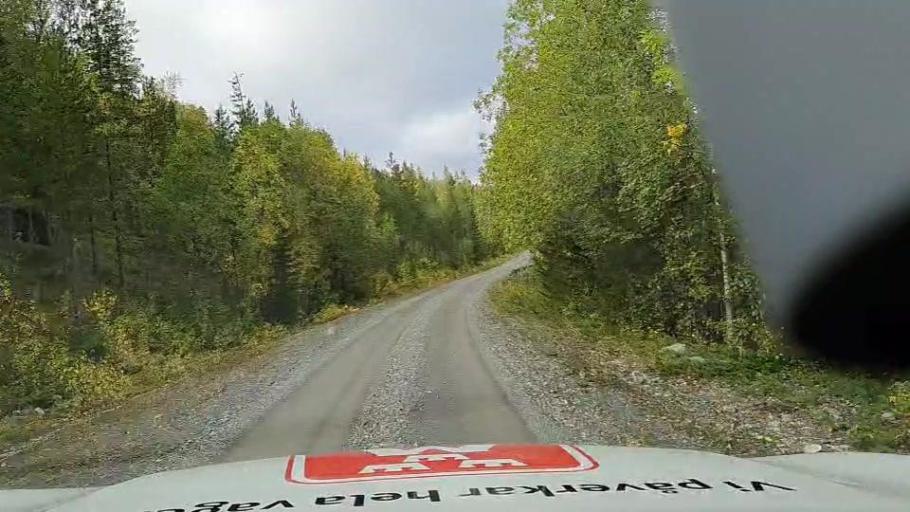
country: SE
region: Jaemtland
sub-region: Are Kommun
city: Jarpen
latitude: 63.1919
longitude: 13.4234
